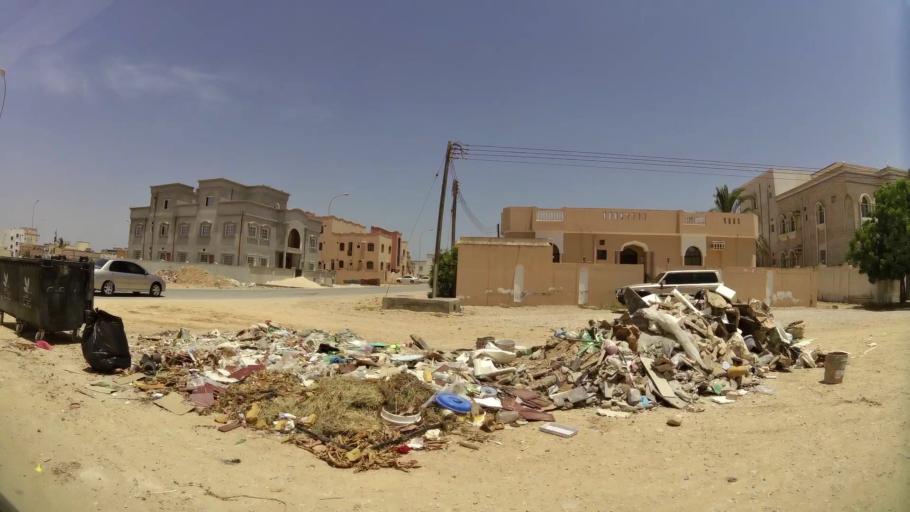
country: OM
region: Zufar
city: Salalah
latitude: 17.0832
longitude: 54.1511
